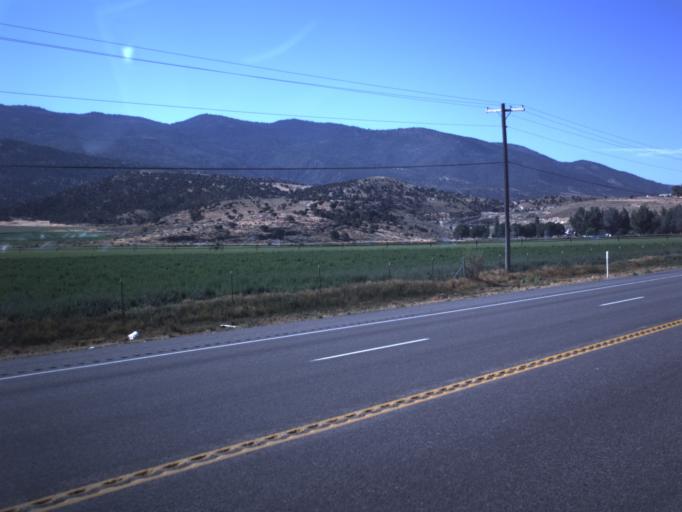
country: US
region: Utah
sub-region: Sanpete County
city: Manti
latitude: 39.2842
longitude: -111.6283
